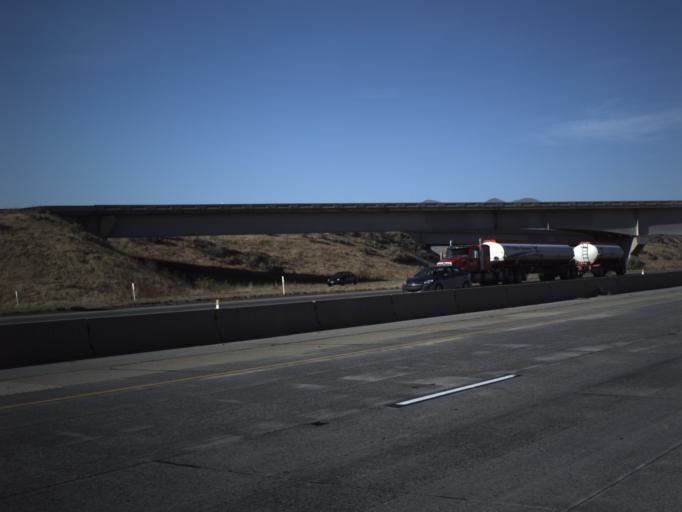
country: US
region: Utah
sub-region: Salt Lake County
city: West Valley City
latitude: 40.7647
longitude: -111.9797
